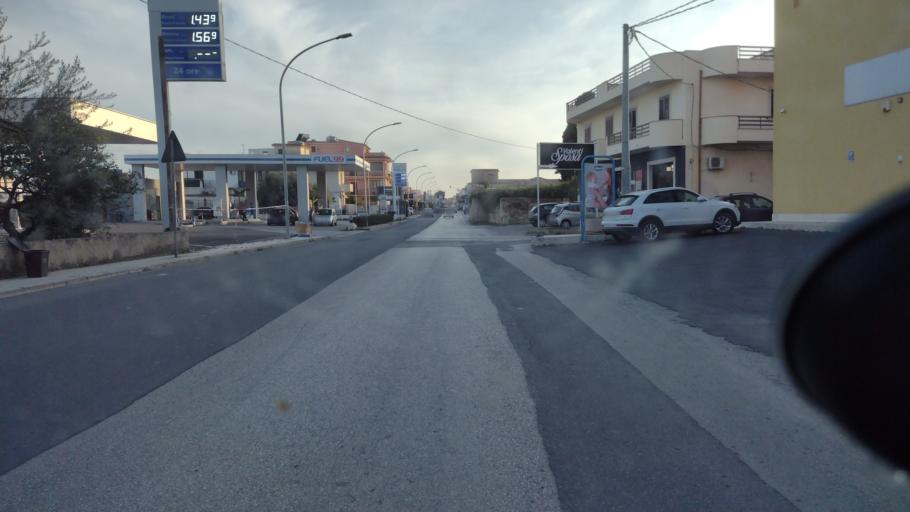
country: IT
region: Sicily
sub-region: Provincia di Siracusa
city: Avola
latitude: 36.9158
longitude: 15.1436
